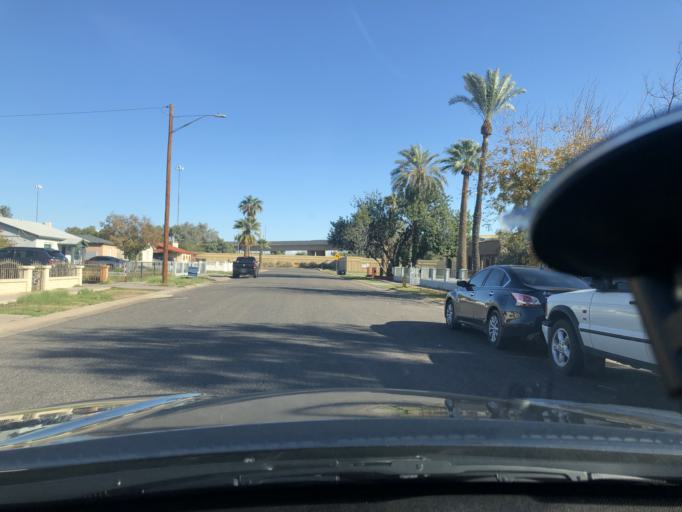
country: US
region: Arizona
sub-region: Maricopa County
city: Phoenix
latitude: 33.4637
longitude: -112.0404
